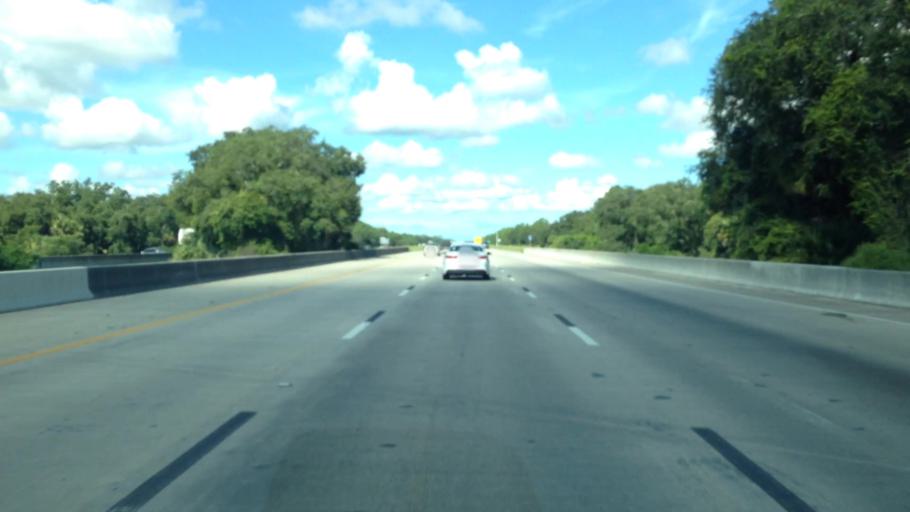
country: US
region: Florida
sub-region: Sarasota County
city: North Port
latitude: 27.1000
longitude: -82.2096
